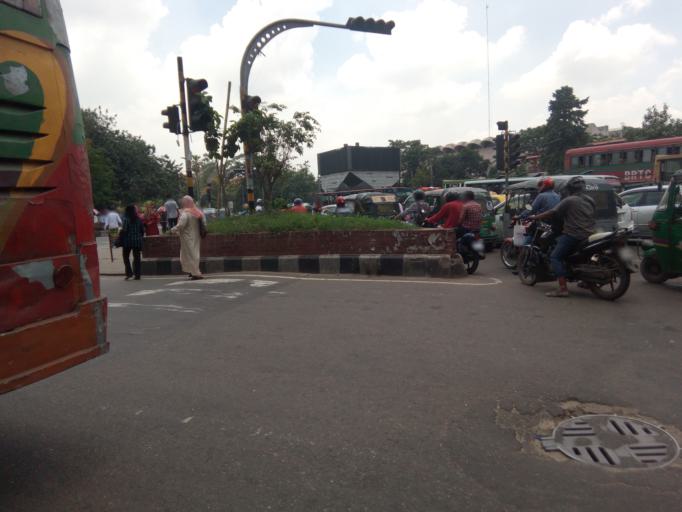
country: BD
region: Dhaka
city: Azimpur
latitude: 23.7384
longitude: 90.3961
